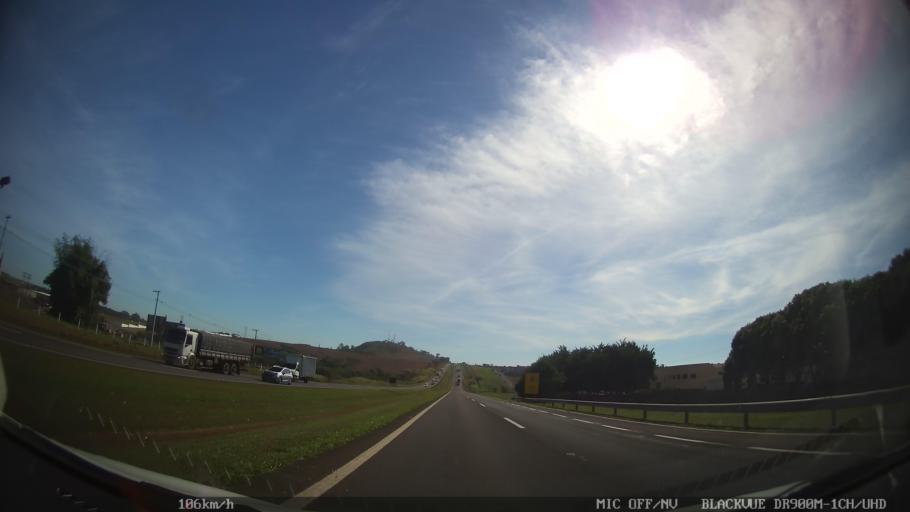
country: BR
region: Sao Paulo
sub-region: Leme
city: Leme
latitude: -22.1724
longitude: -47.3988
